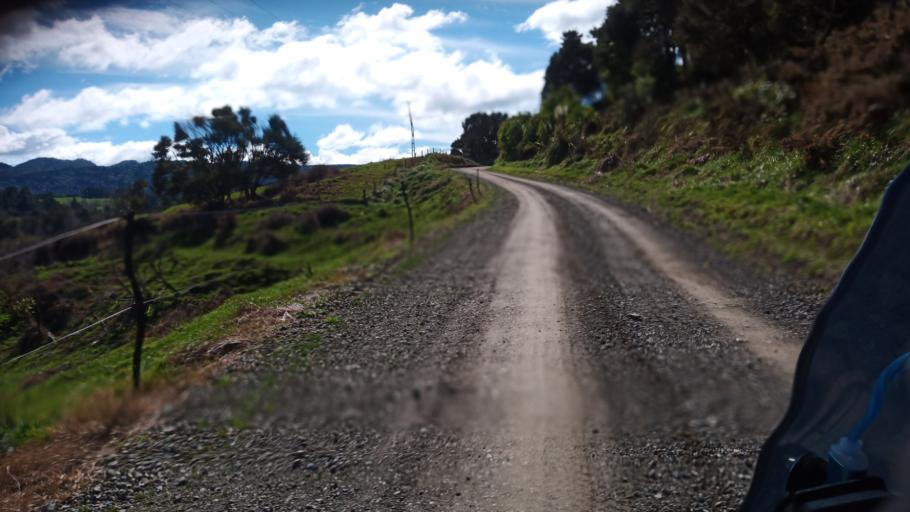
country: NZ
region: Hawke's Bay
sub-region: Wairoa District
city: Wairoa
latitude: -38.8272
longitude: 177.1623
